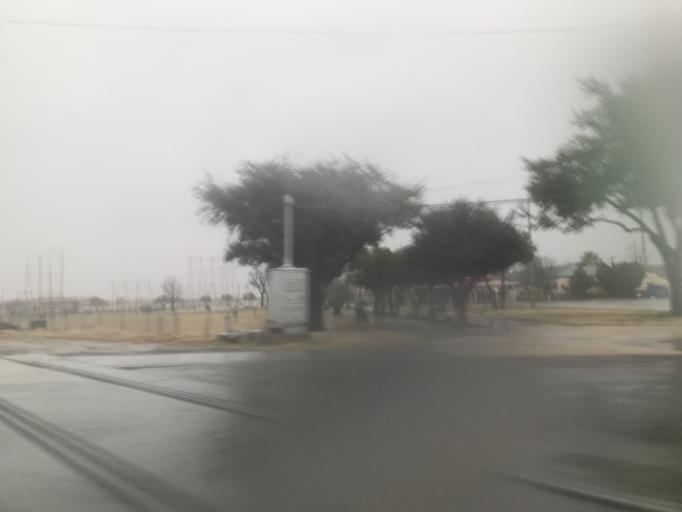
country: US
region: Texas
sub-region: Tom Green County
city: San Angelo
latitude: 31.4539
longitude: -100.4346
